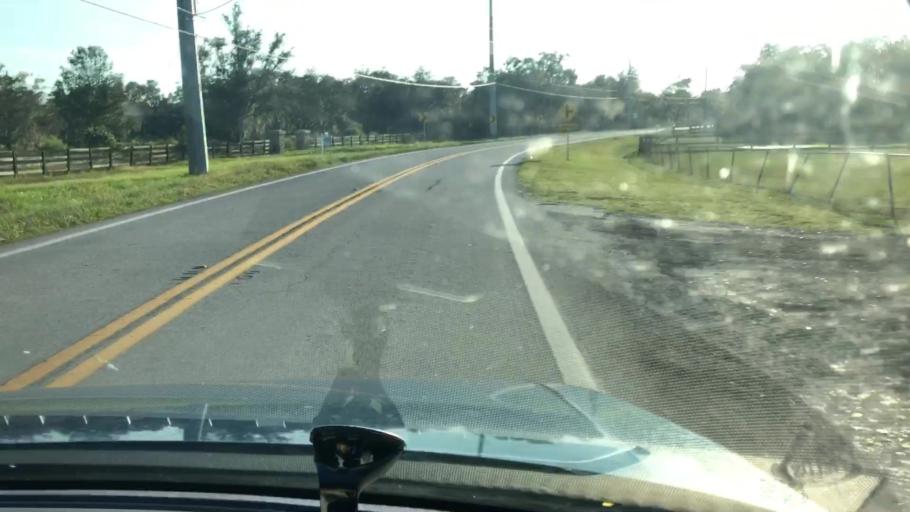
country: US
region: Florida
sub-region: Polk County
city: Gibsonia
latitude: 28.1545
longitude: -81.9183
